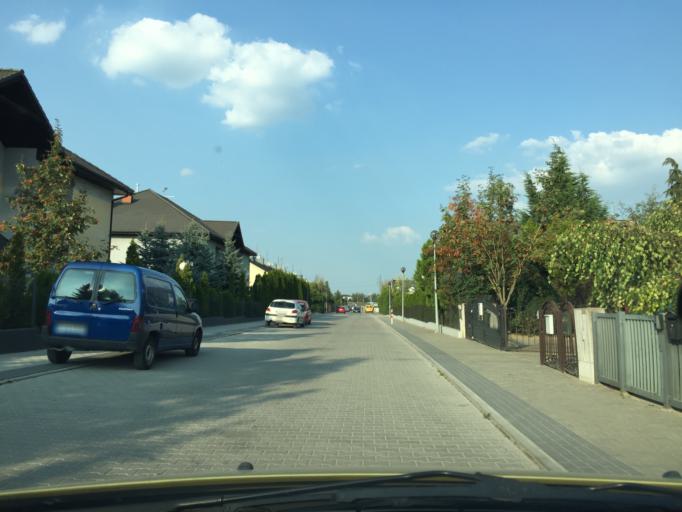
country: PL
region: Greater Poland Voivodeship
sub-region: Powiat poznanski
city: Plewiska
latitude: 52.3740
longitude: 16.8139
